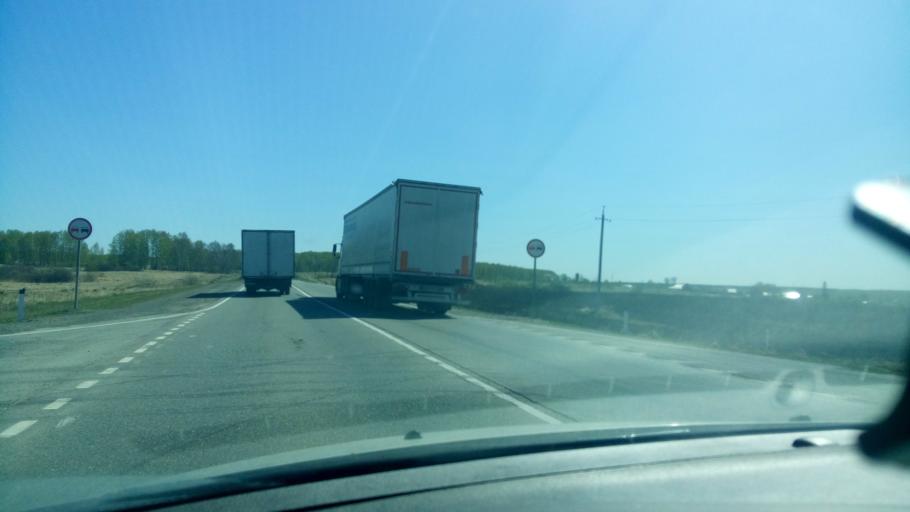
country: RU
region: Sverdlovsk
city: Bogdanovich
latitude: 56.7557
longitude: 62.2149
